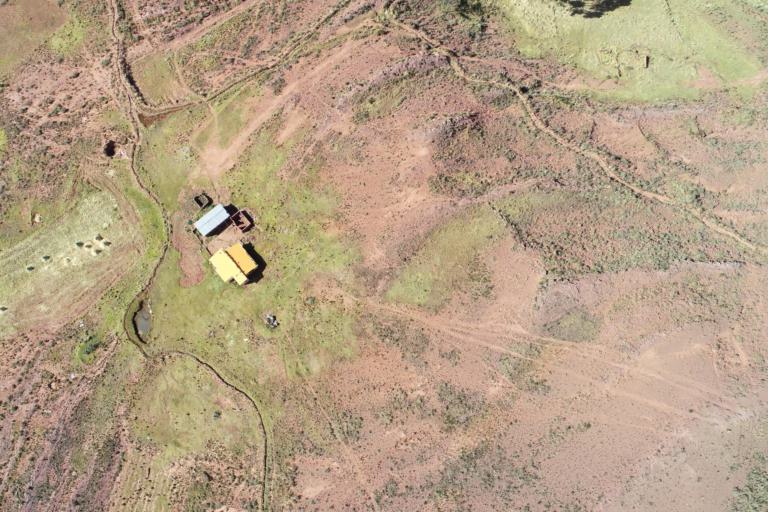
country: BO
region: La Paz
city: Tiahuanaco
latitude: -16.5996
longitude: -68.7603
